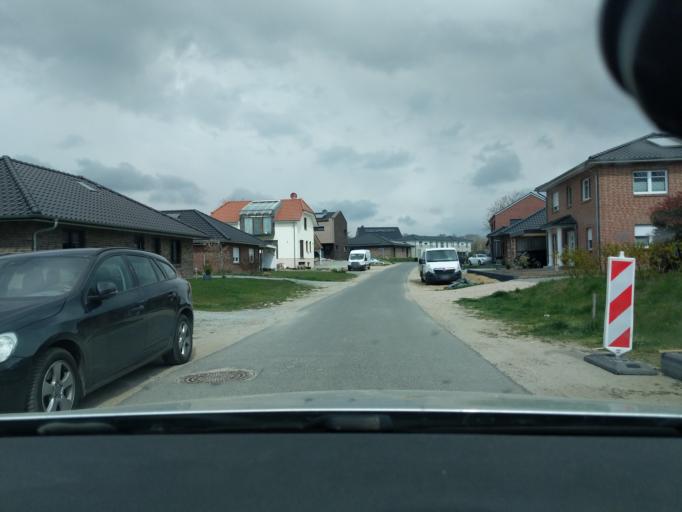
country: DE
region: Lower Saxony
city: Stade
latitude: 53.5700
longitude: 9.4673
